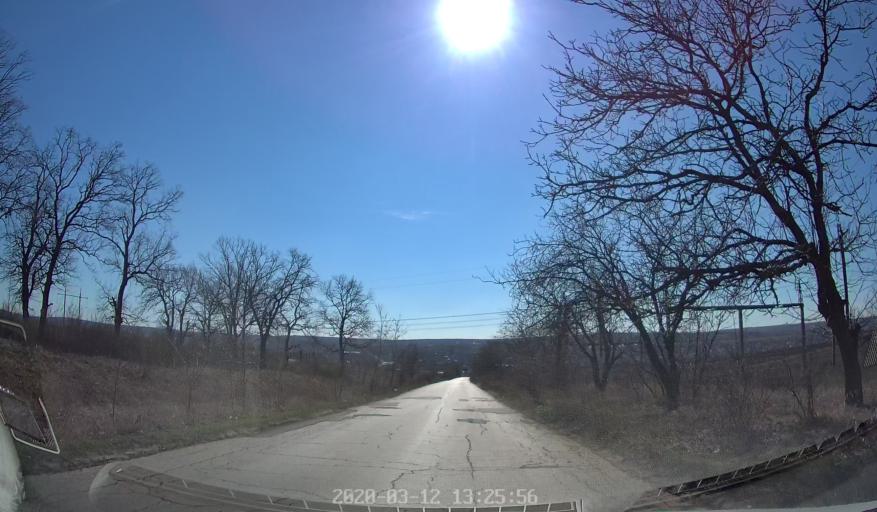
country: MD
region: Laloveni
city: Ialoveni
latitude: 46.9390
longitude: 28.8174
